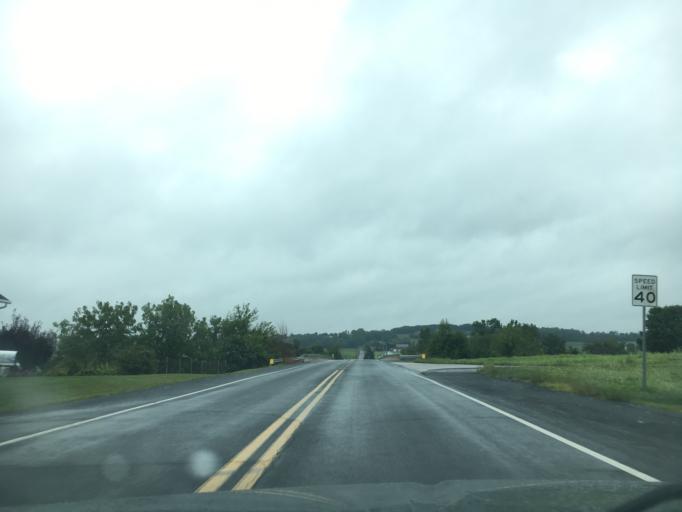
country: US
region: Pennsylvania
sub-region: Berks County
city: Kutztown
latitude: 40.5036
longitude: -75.8044
